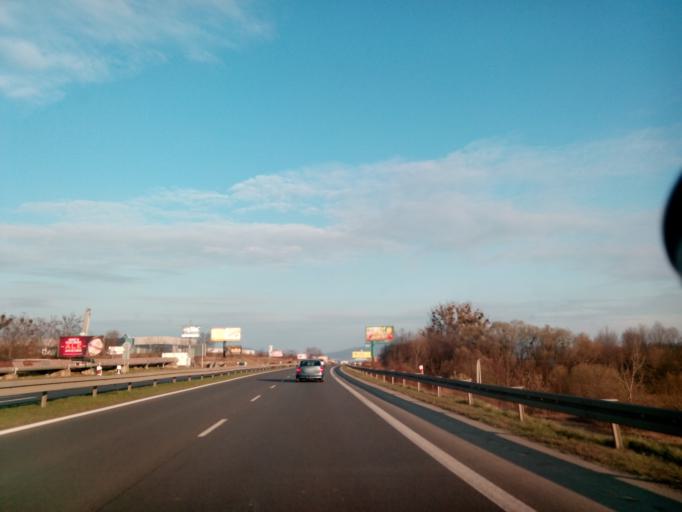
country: SK
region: Kosicky
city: Kosice
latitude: 48.6922
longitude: 21.2395
